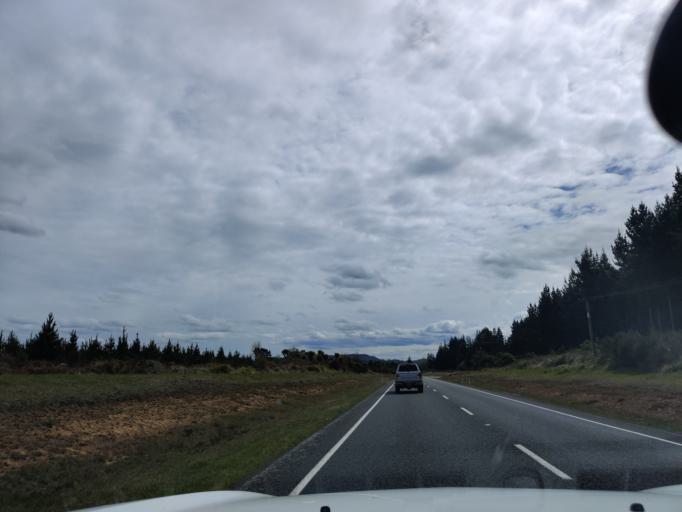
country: NZ
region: Manawatu-Wanganui
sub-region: Ruapehu District
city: Waiouru
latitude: -39.4758
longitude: 175.5214
